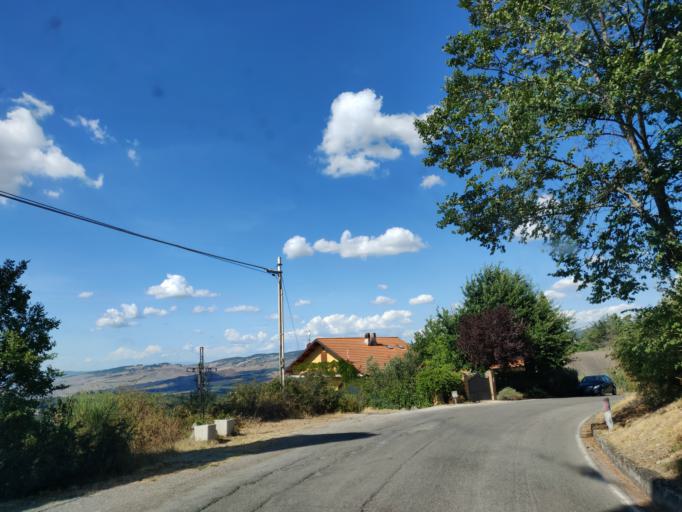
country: IT
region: Tuscany
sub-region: Provincia di Siena
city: Radicofani
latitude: 42.9735
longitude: 11.7376
